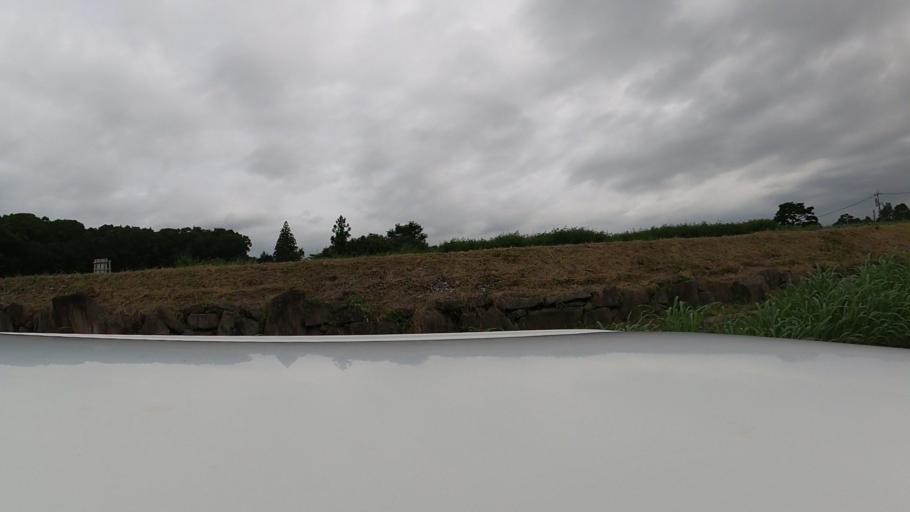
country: JP
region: Kumamoto
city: Ozu
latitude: 32.8317
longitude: 130.8642
